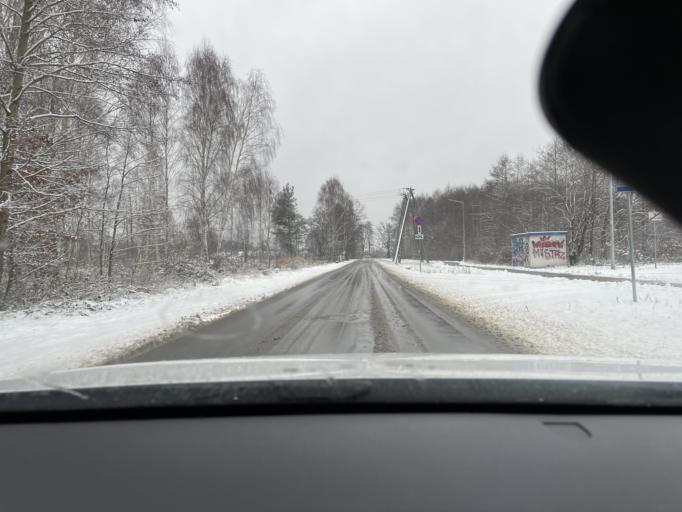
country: PL
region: Masovian Voivodeship
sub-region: Powiat zyrardowski
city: Zyrardow
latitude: 52.0370
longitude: 20.4504
